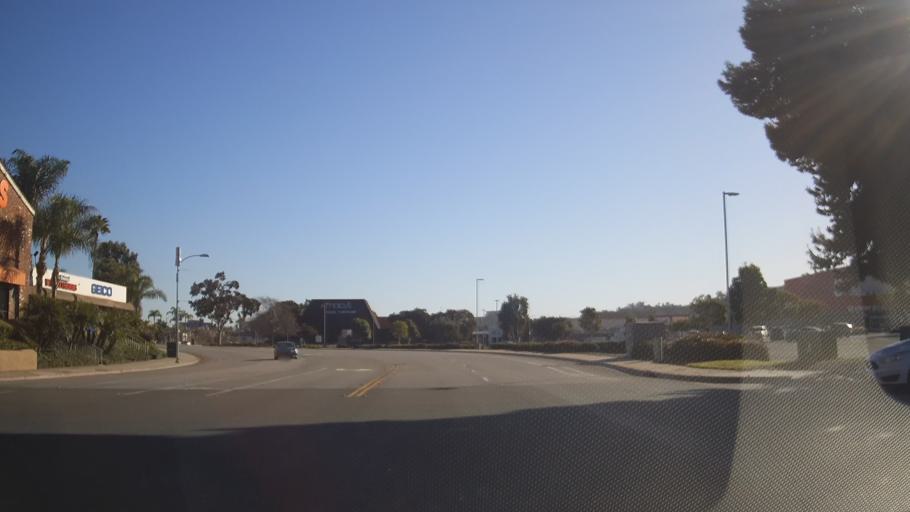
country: US
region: California
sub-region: San Diego County
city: San Diego
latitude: 32.7690
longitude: -117.1522
